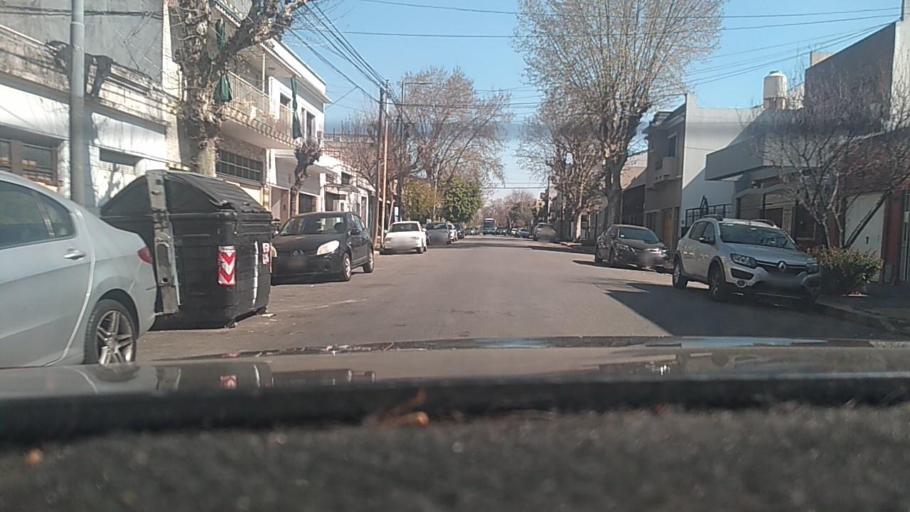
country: AR
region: Buenos Aires F.D.
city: Villa Santa Rita
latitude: -34.6076
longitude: -58.4953
